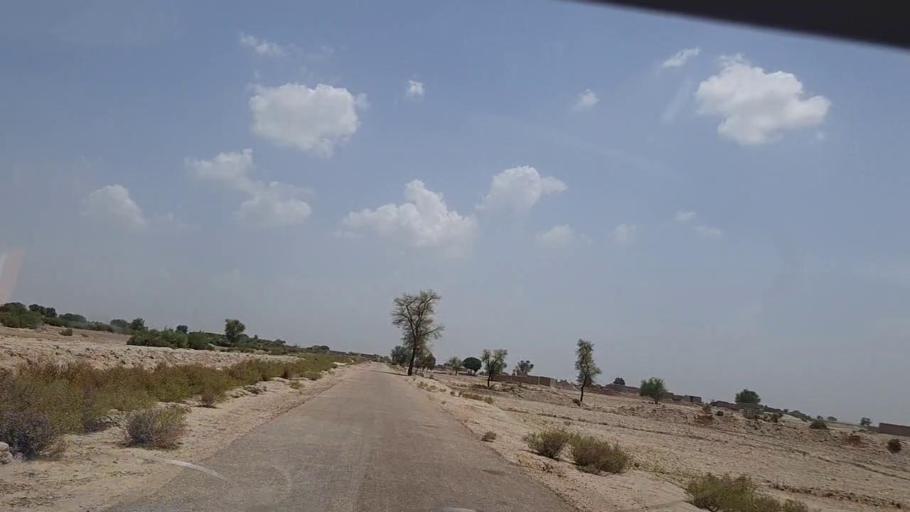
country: PK
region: Sindh
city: Bhan
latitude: 26.5257
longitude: 67.6342
